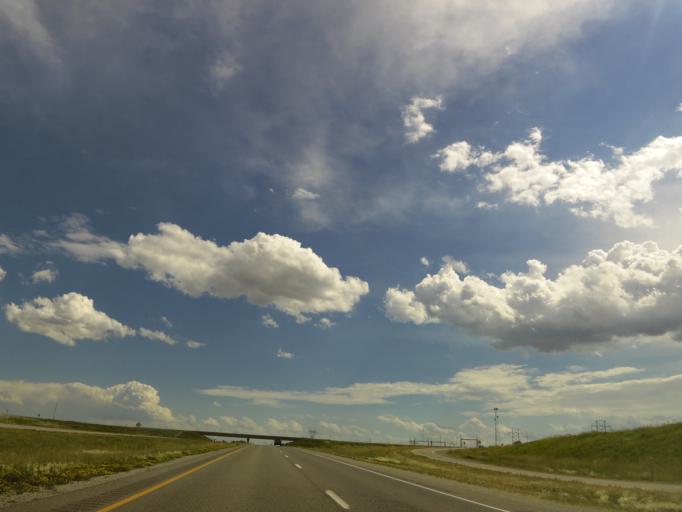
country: US
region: Iowa
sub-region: Washington County
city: Washington
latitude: 41.3406
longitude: -91.5524
